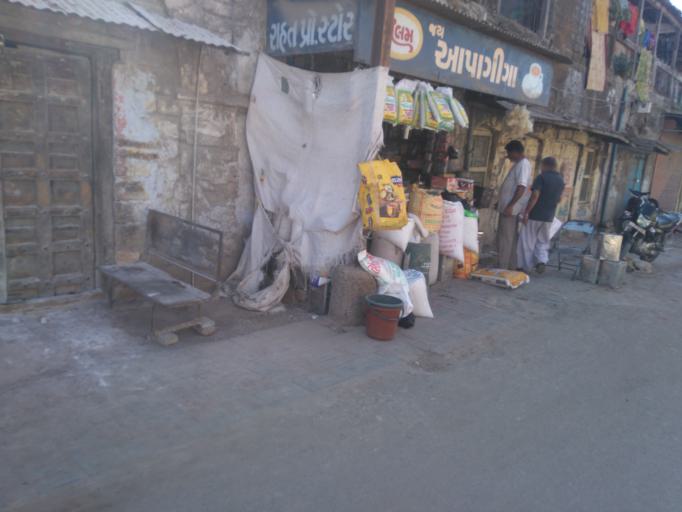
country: IN
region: Gujarat
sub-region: Junagadh
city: Junagadh
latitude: 21.5290
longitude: 70.4640
